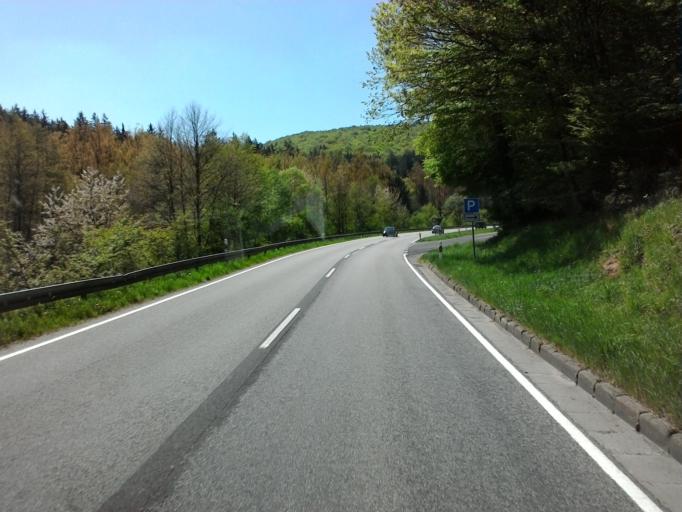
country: DE
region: Bavaria
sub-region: Regierungsbezirk Unterfranken
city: Rechtenbach
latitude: 49.9723
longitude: 9.5356
